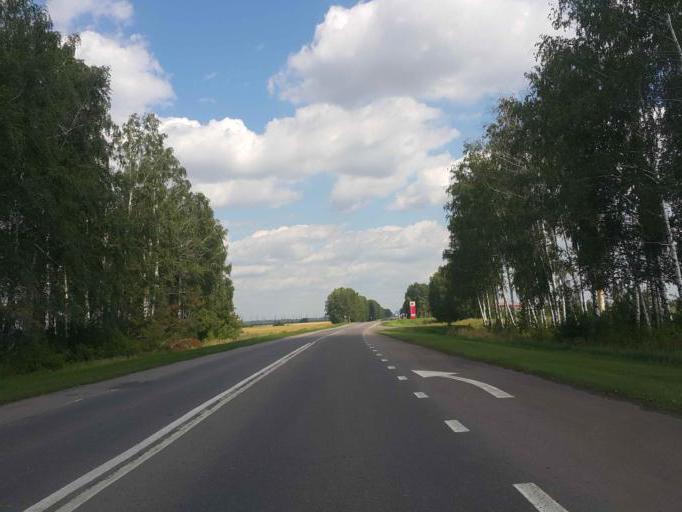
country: RU
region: Tambov
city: Goreloye
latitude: 53.0399
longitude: 41.4669
